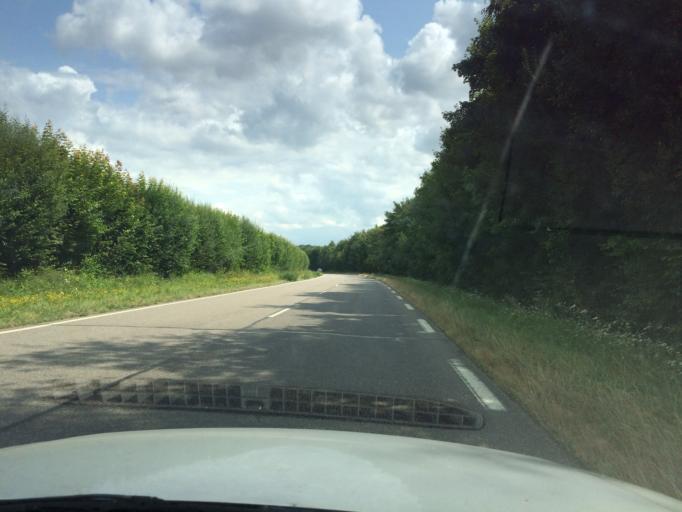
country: FR
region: Lower Normandy
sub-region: Departement du Calvados
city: Le Molay-Littry
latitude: 49.3338
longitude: -0.9171
